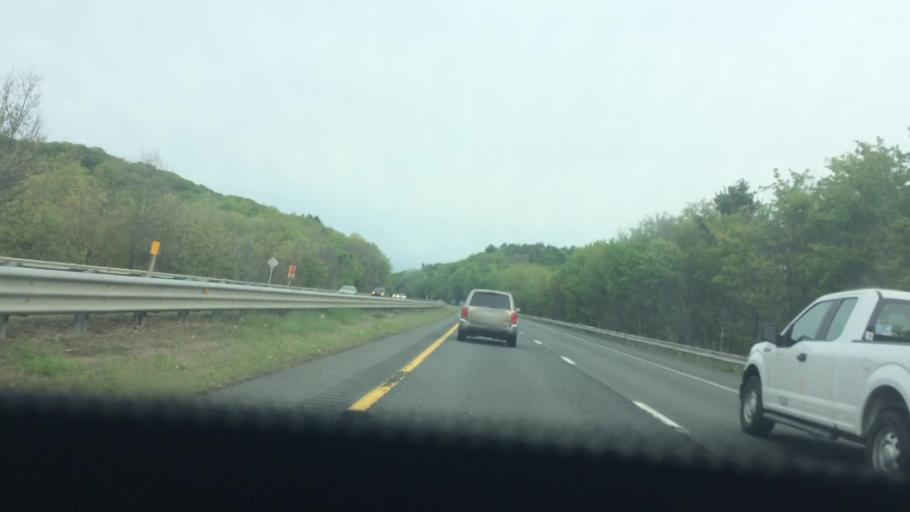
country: US
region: Massachusetts
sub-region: Worcester County
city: Fiskdale
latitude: 42.1479
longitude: -72.1453
